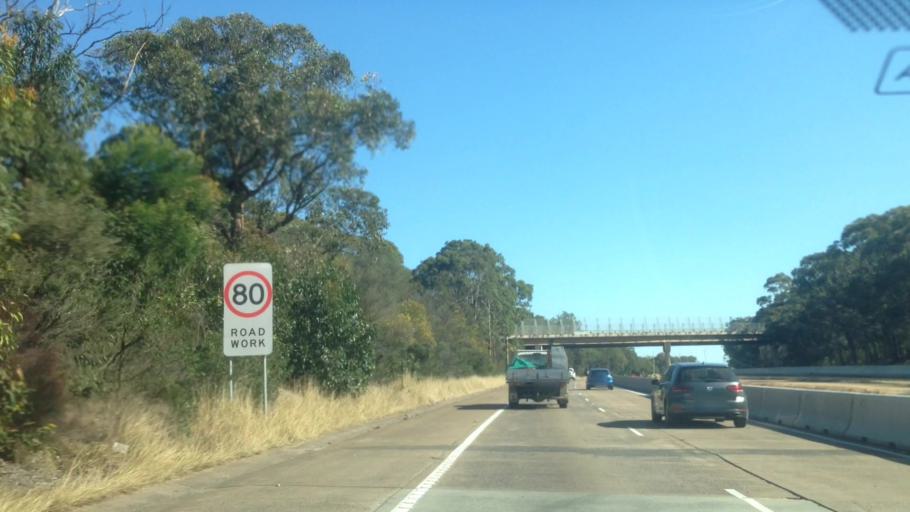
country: AU
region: New South Wales
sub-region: Wyong Shire
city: Jilliby
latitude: -33.2143
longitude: 151.4497
